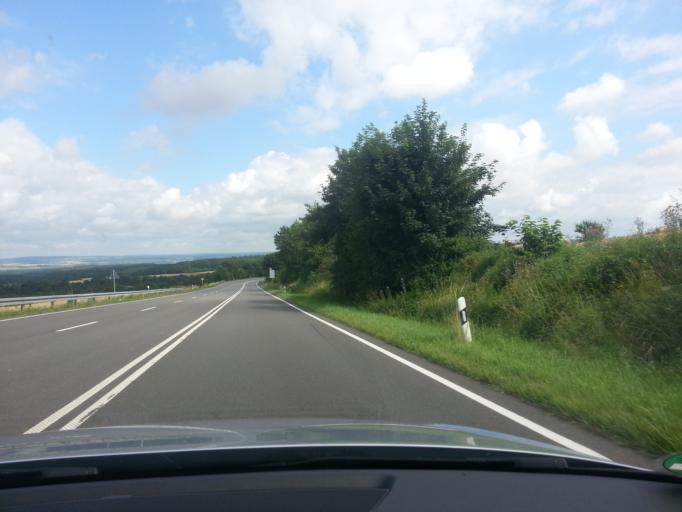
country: DE
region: Rheinland-Pfalz
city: Kirf
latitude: 49.5271
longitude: 6.4360
